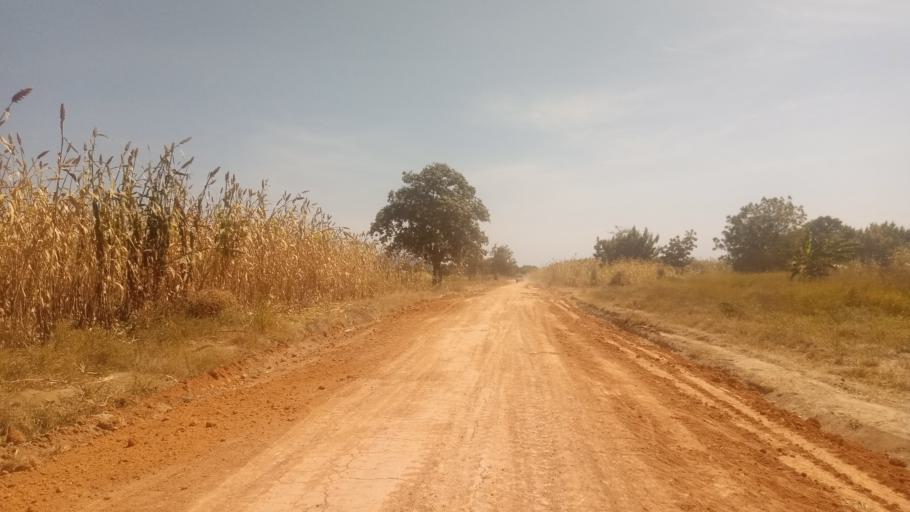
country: NG
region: Adamawa
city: Madagali
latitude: 10.8469
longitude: 13.3934
